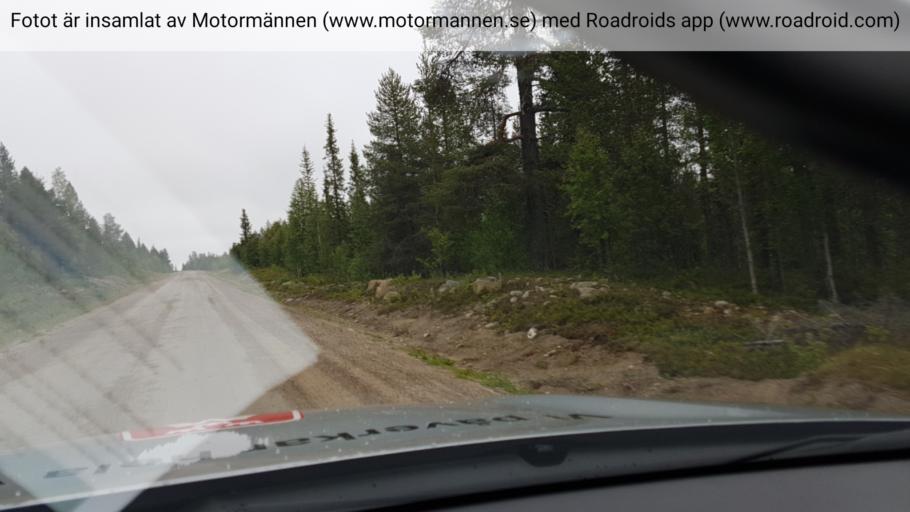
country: SE
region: Norrbotten
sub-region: Gallivare Kommun
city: Gaellivare
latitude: 66.7439
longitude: 20.6721
